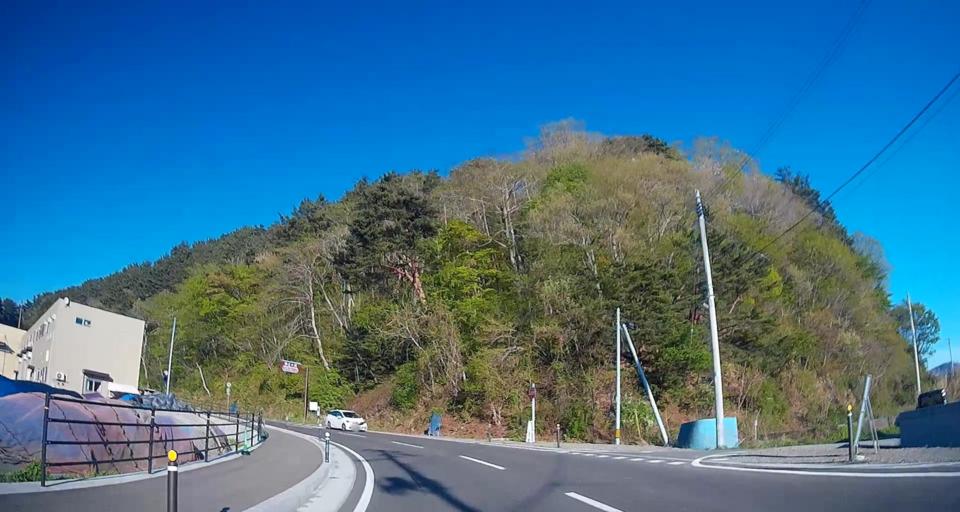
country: JP
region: Iwate
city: Miyako
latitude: 39.6448
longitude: 141.9750
